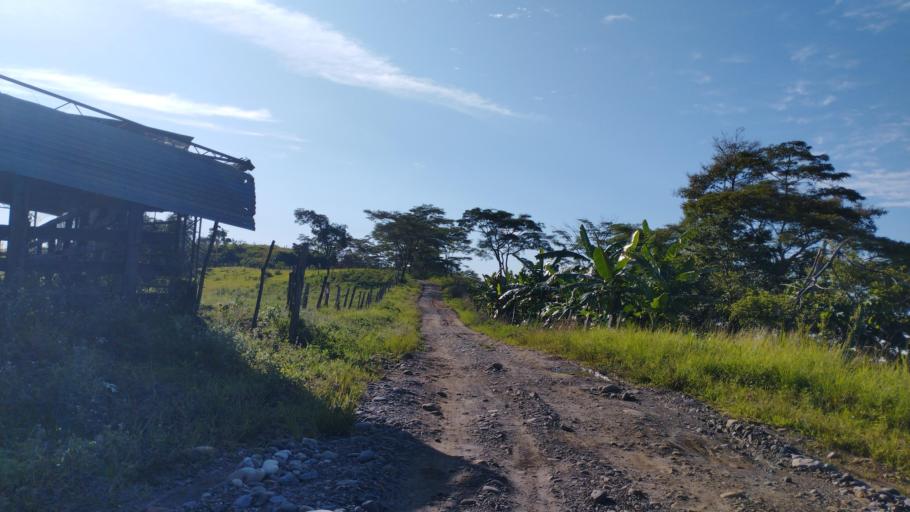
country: CO
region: Casanare
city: Sabanalarga
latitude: 4.7862
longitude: -73.0875
